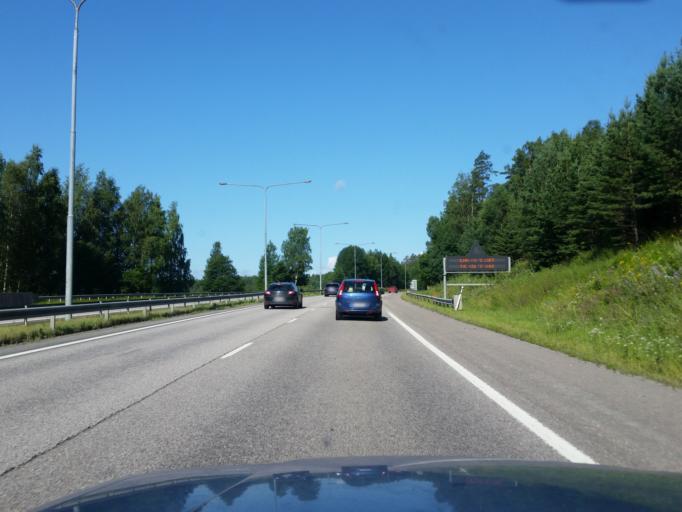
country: FI
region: Uusimaa
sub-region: Helsinki
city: Espoo
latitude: 60.2239
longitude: 24.6189
